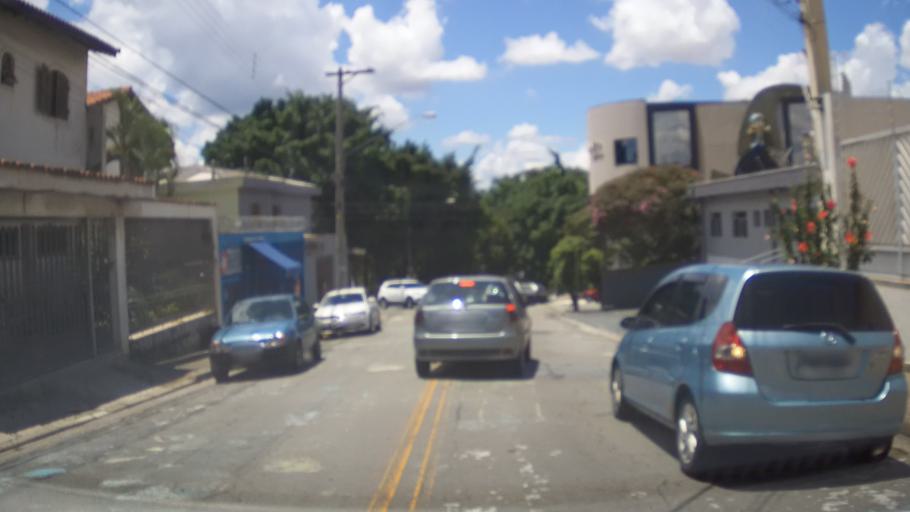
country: BR
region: Sao Paulo
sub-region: Guarulhos
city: Guarulhos
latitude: -23.4515
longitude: -46.5363
